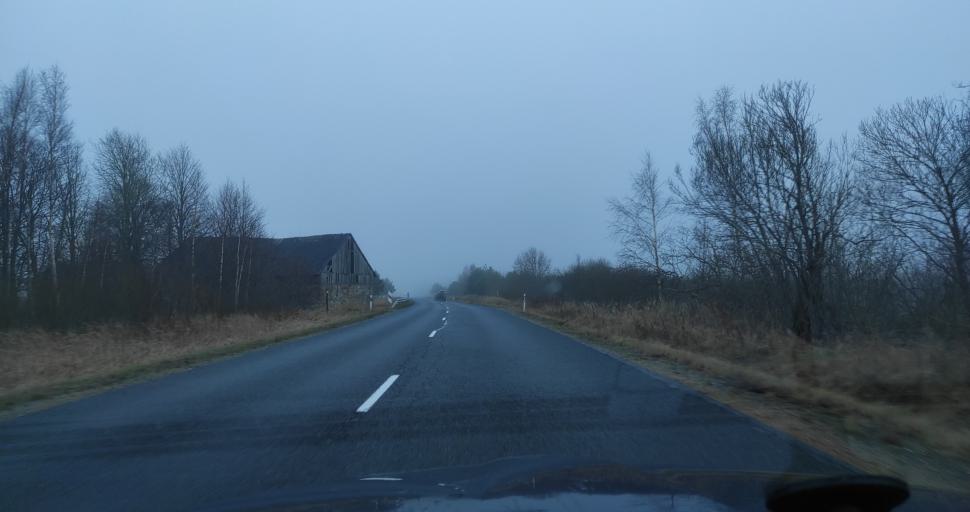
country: LV
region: Alsunga
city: Alsunga
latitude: 57.1136
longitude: 21.4230
